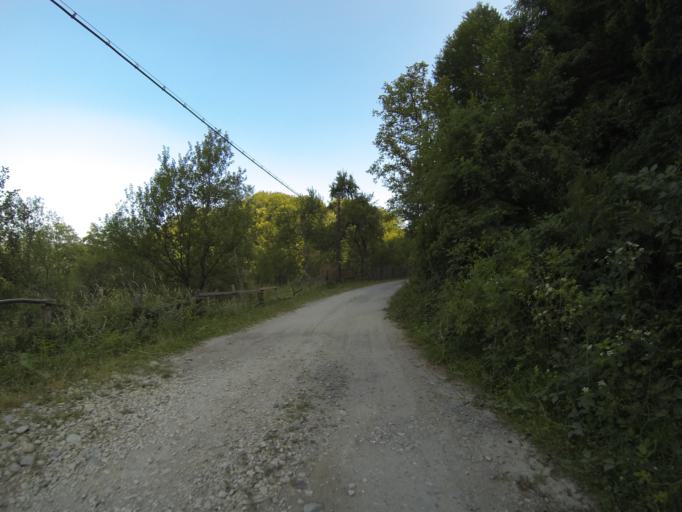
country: RO
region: Valcea
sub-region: Comuna Horezu
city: Horezu
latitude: 45.1822
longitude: 23.9924
